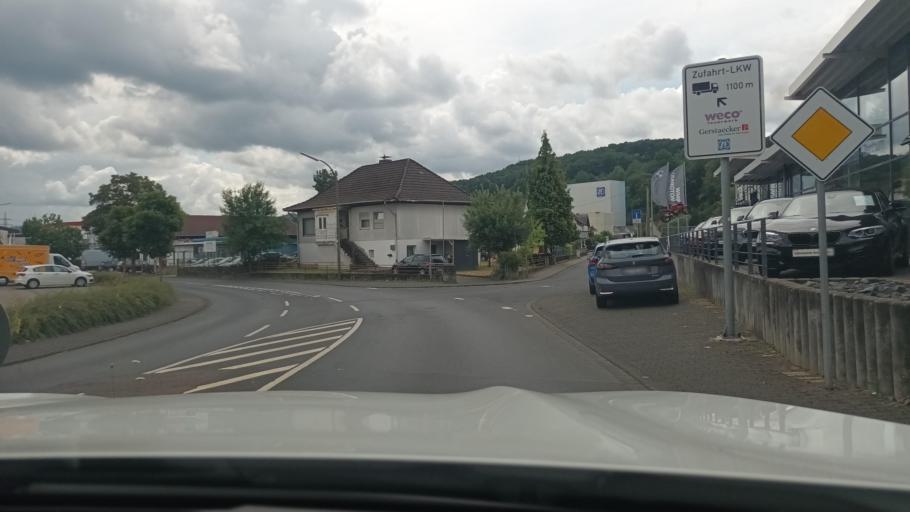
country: DE
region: North Rhine-Westphalia
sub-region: Regierungsbezirk Koln
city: Eitorf
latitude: 50.7722
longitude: 7.4622
